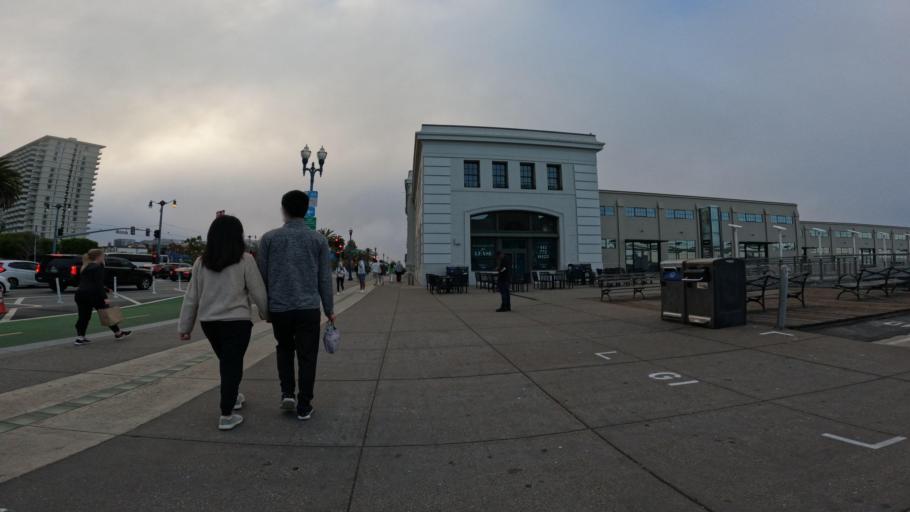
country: US
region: California
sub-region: San Francisco County
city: San Francisco
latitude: 37.7964
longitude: -122.3947
